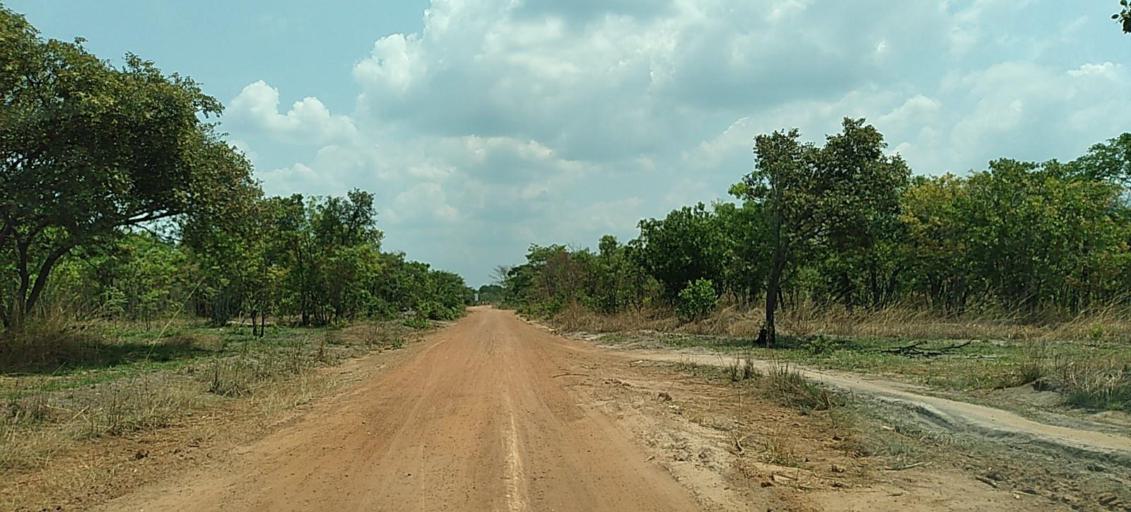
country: ZM
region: Copperbelt
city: Luanshya
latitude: -13.1509
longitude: 28.3150
